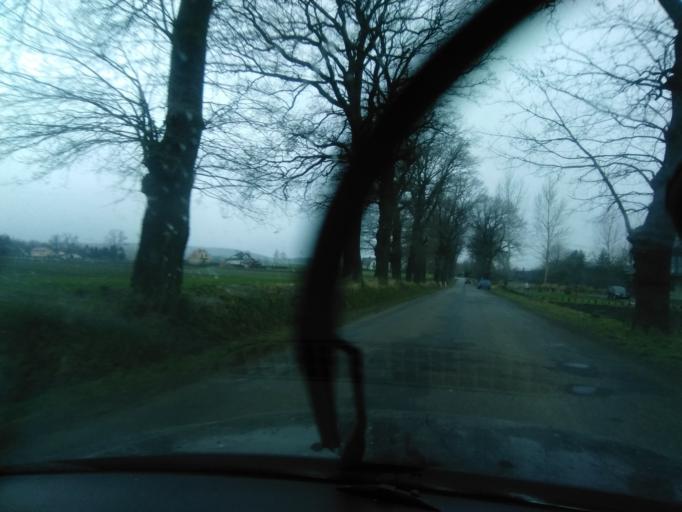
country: PL
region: Subcarpathian Voivodeship
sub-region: Powiat jaroslawski
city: Pruchnik
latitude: 49.9037
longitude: 22.5538
